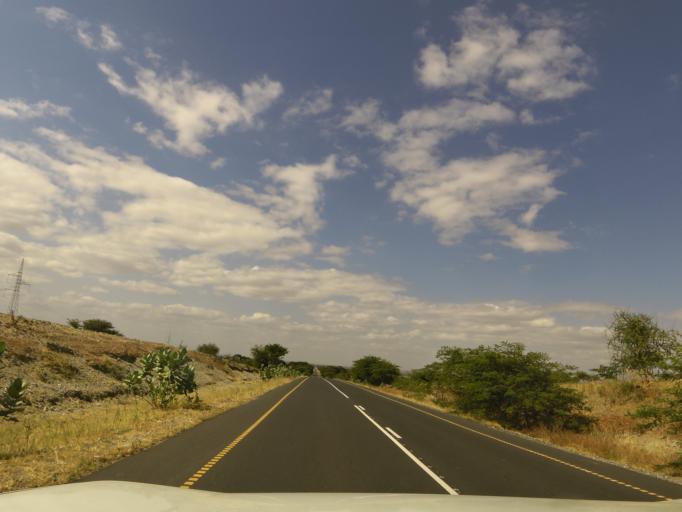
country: TZ
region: Arusha
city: Mto wa Mbu
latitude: -3.6730
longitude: 35.9449
